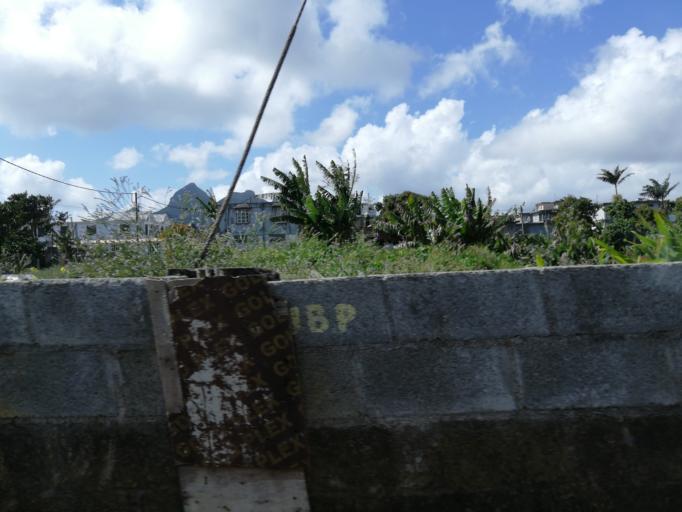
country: MU
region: Moka
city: Verdun
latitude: -20.2179
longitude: 57.5380
